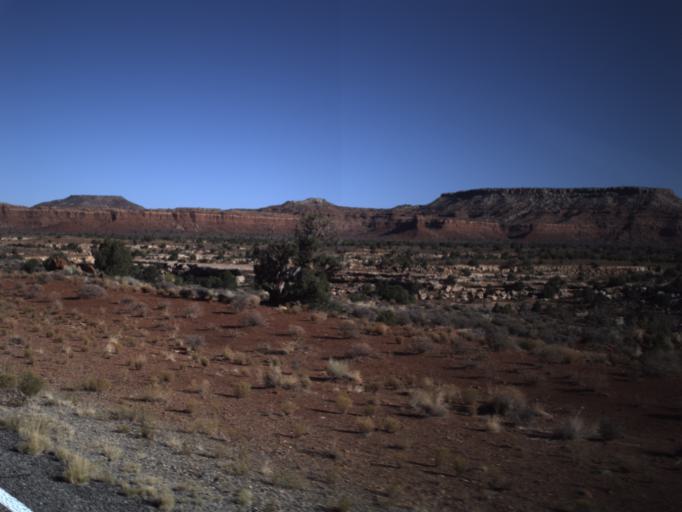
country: US
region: Utah
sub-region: San Juan County
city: Blanding
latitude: 37.6894
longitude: -110.2244
